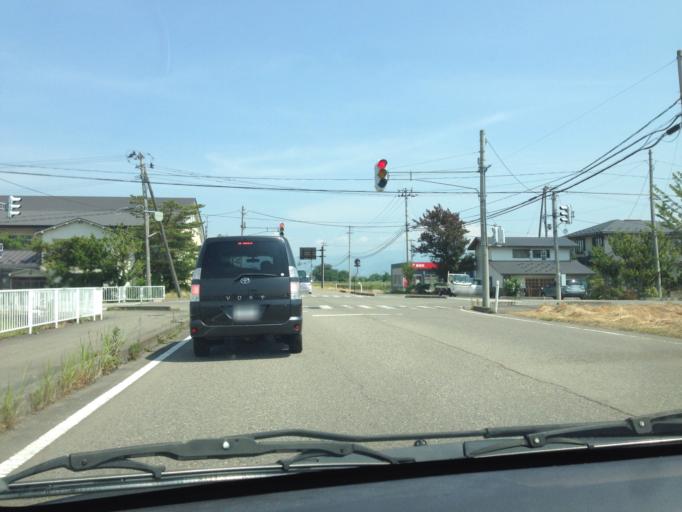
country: JP
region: Fukushima
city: Kitakata
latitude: 37.5639
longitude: 139.8888
